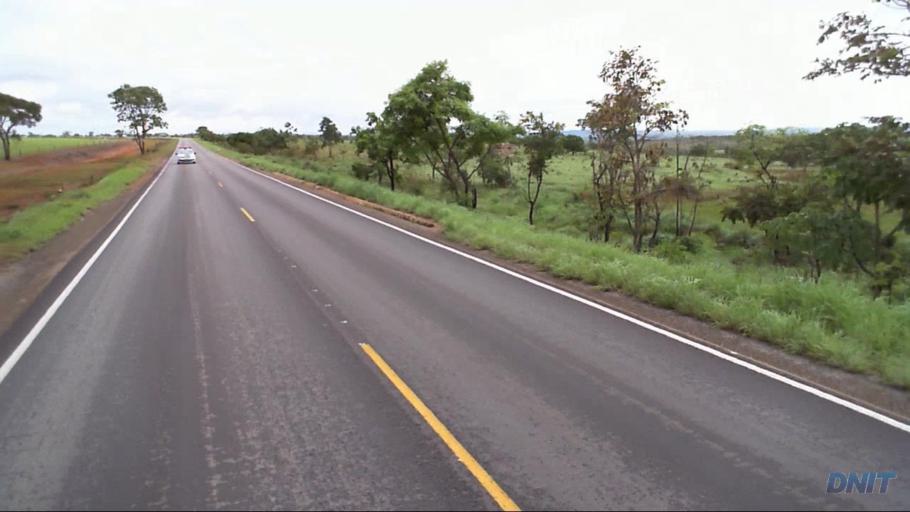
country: BR
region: Goias
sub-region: Padre Bernardo
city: Padre Bernardo
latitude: -15.3138
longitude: -48.2282
